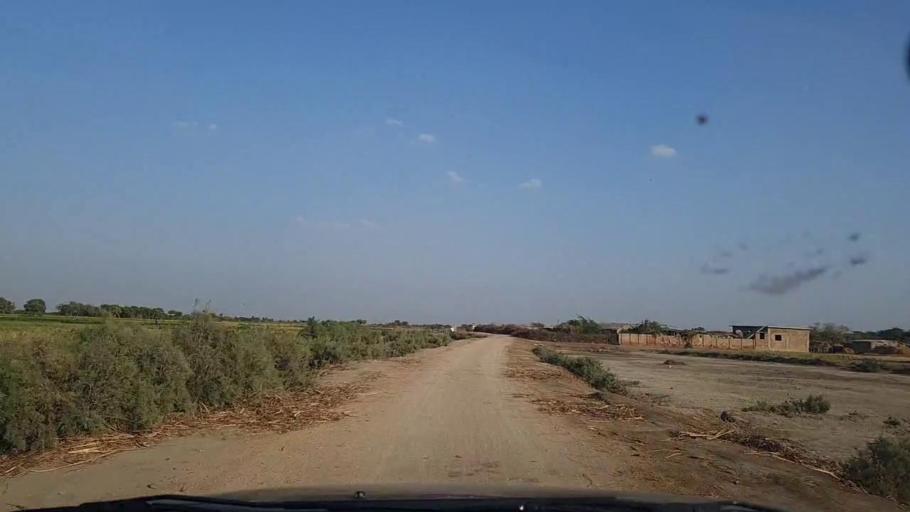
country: PK
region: Sindh
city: Daro Mehar
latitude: 24.7482
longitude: 68.0923
